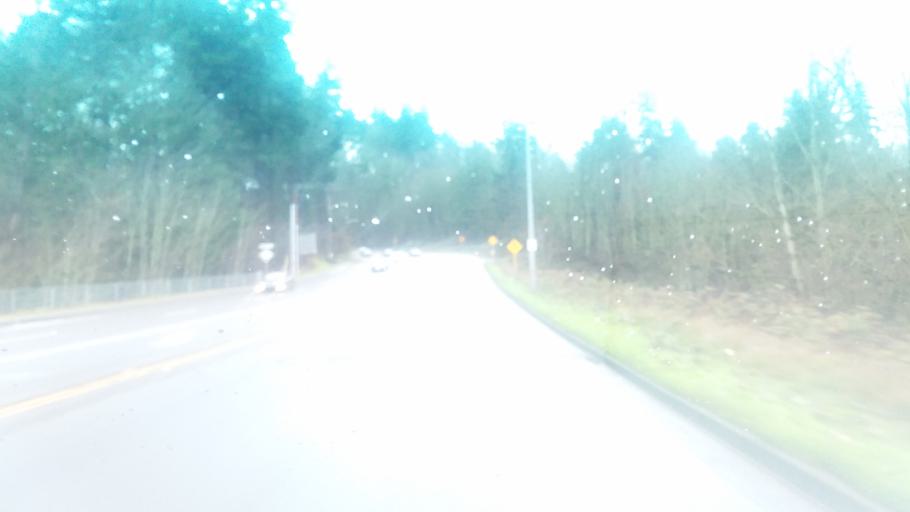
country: US
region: Washington
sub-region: King County
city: Kent
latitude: 47.4121
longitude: -122.2179
